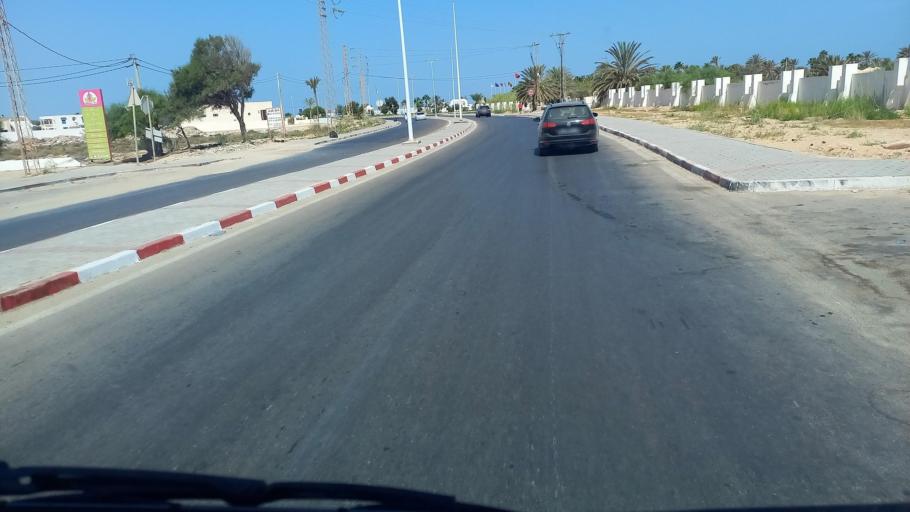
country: TN
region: Madanin
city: Midoun
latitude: 33.8676
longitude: 10.9593
